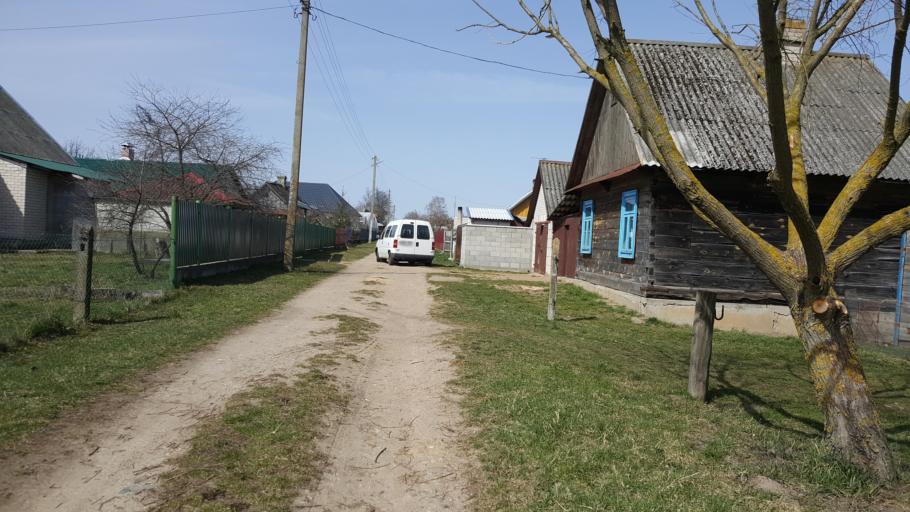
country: BY
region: Brest
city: Kamyanyets
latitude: 52.4658
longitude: 23.7187
